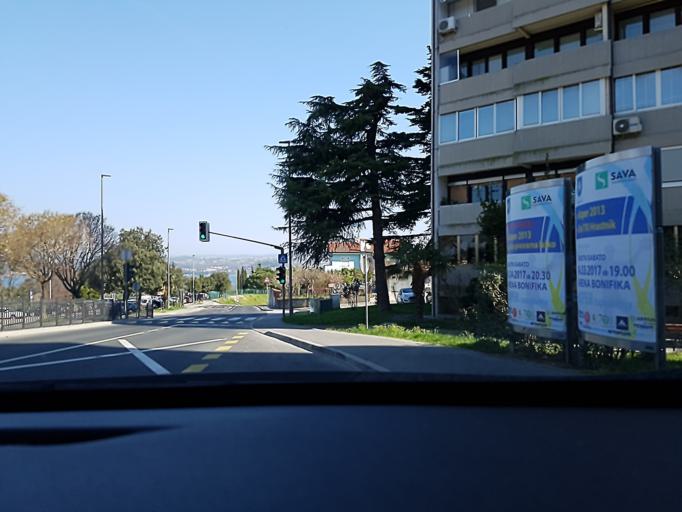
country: SI
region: Koper-Capodistria
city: Koper
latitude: 45.5423
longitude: 13.7119
